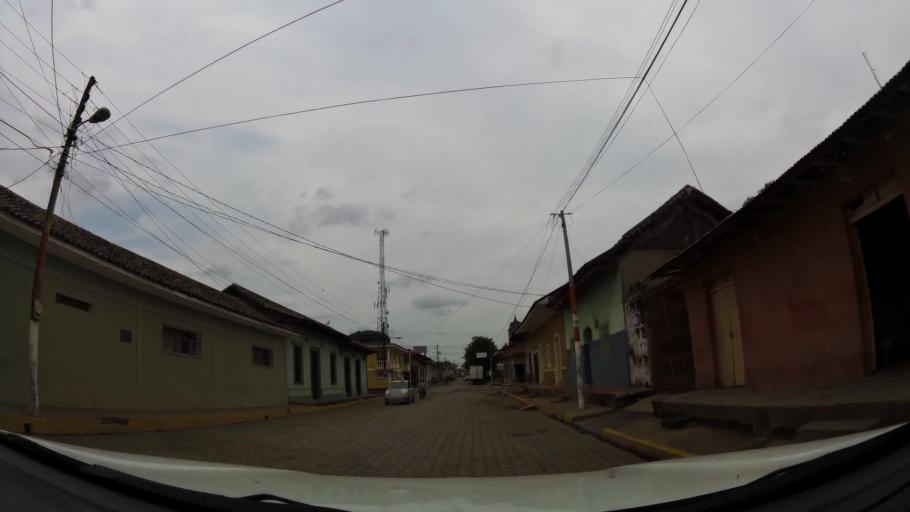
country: NI
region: Granada
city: Nandaime
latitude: 11.7561
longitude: -86.0506
